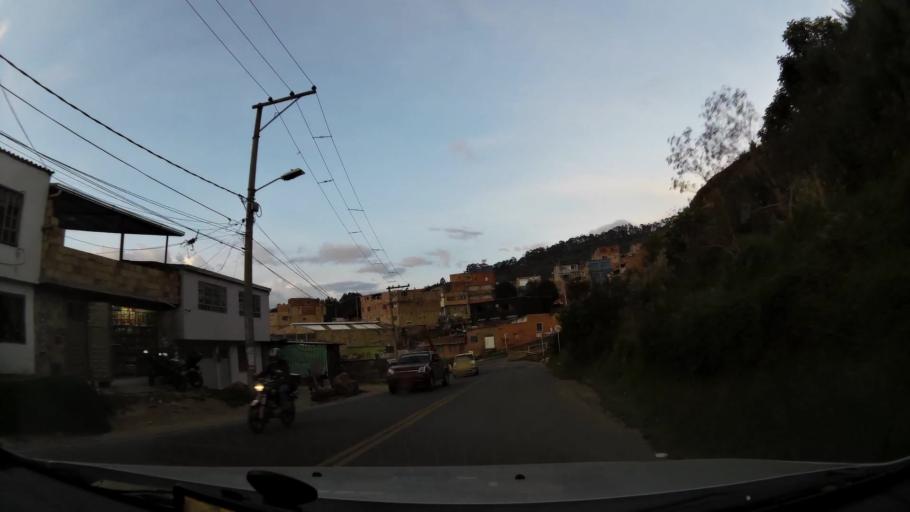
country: CO
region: Bogota D.C.
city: Bogota
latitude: 4.5430
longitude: -74.0836
